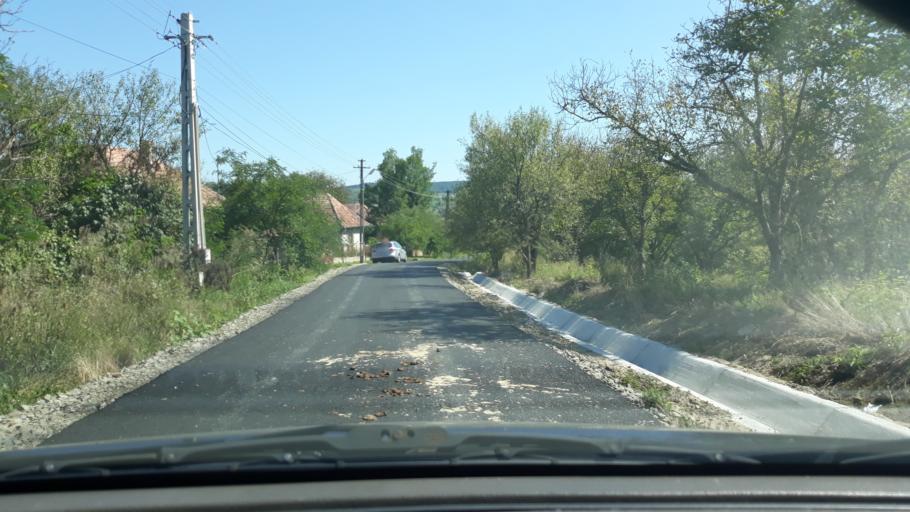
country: RO
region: Salaj
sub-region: Comuna Dobrin
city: Dobrin
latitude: 47.2917
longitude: 23.0914
